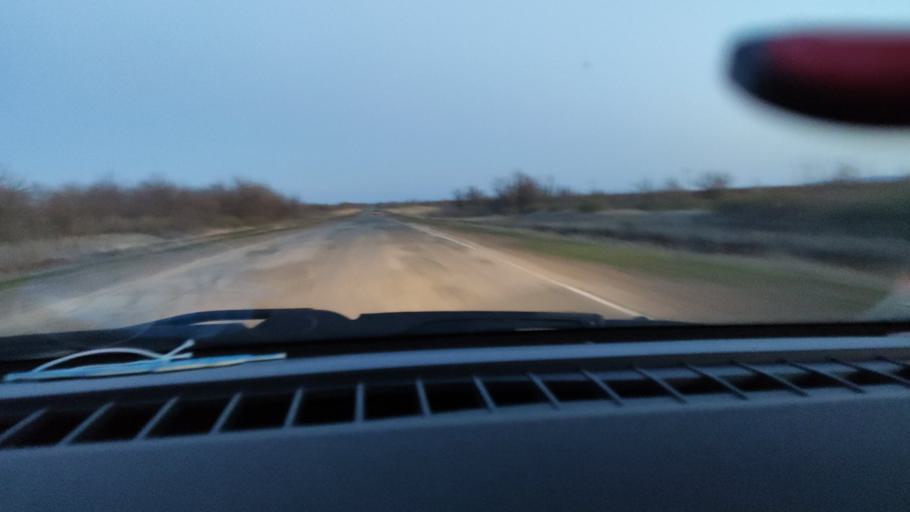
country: RU
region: Saratov
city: Rovnoye
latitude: 51.0088
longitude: 46.0996
